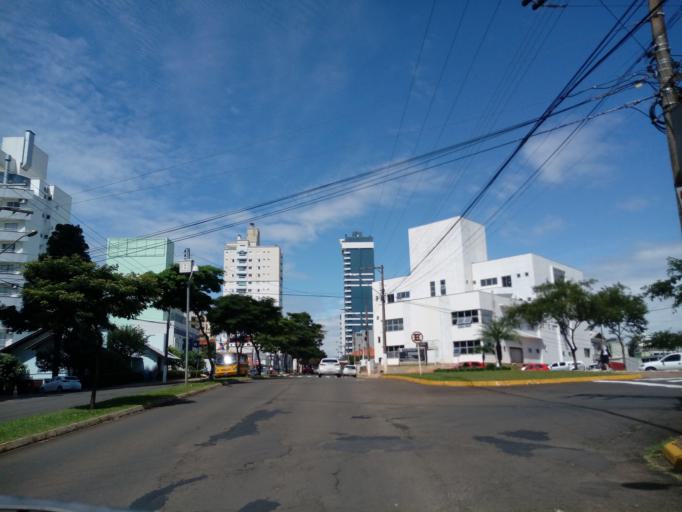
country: BR
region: Santa Catarina
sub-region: Chapeco
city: Chapeco
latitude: -27.1008
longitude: -52.6119
